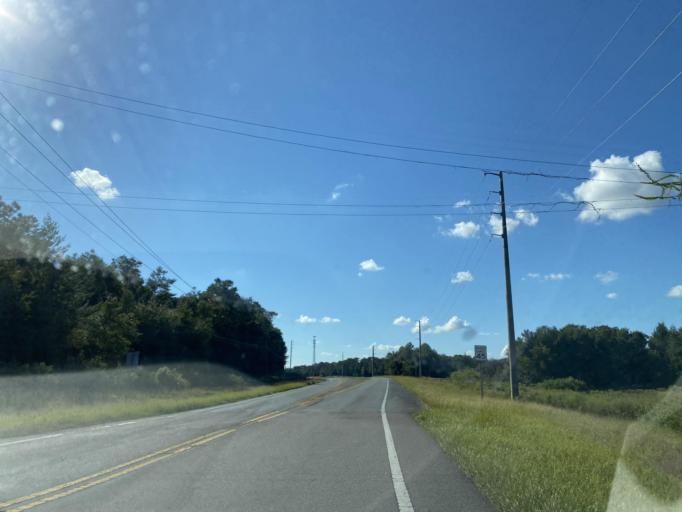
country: US
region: Florida
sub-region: Citrus County
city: Hernando
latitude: 29.0532
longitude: -82.2769
